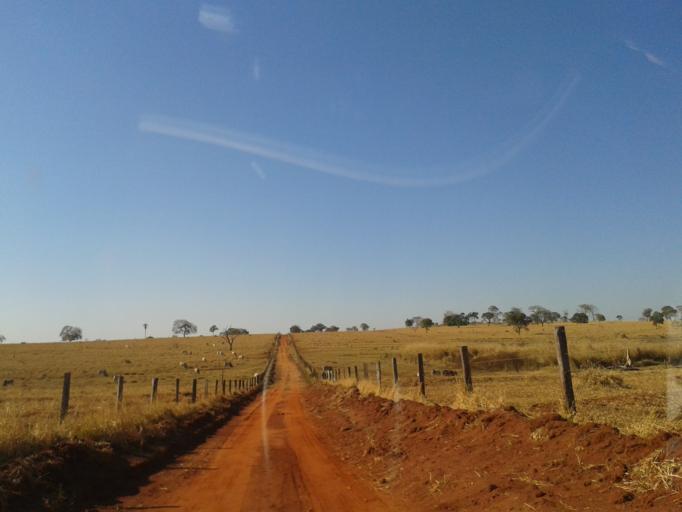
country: BR
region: Minas Gerais
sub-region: Santa Vitoria
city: Santa Vitoria
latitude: -19.0511
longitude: -49.9351
